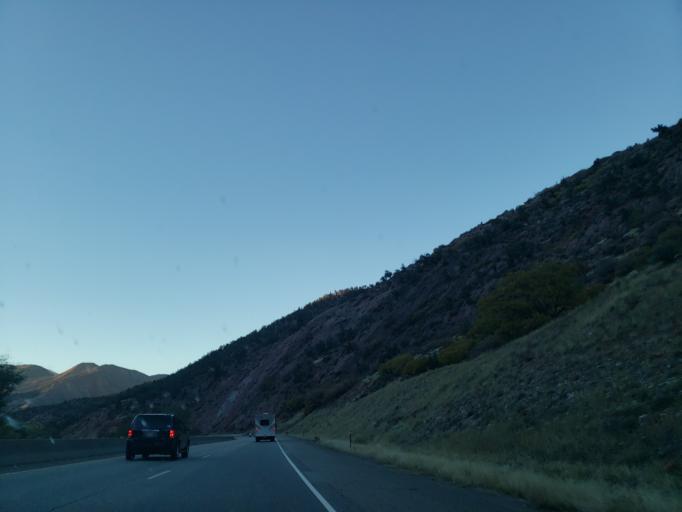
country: US
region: Colorado
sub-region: Garfield County
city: Glenwood Springs
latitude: 39.5686
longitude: -107.4266
